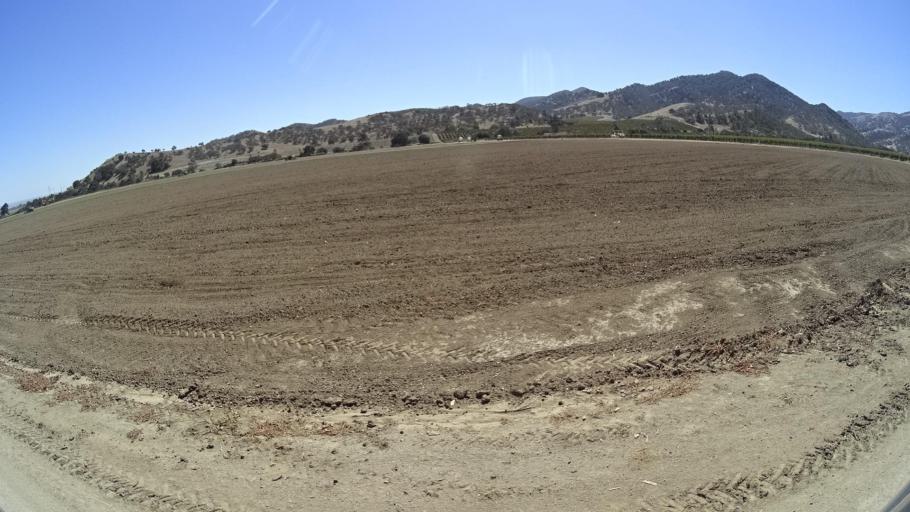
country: US
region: California
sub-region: Monterey County
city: King City
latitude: 36.2283
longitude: -121.1847
